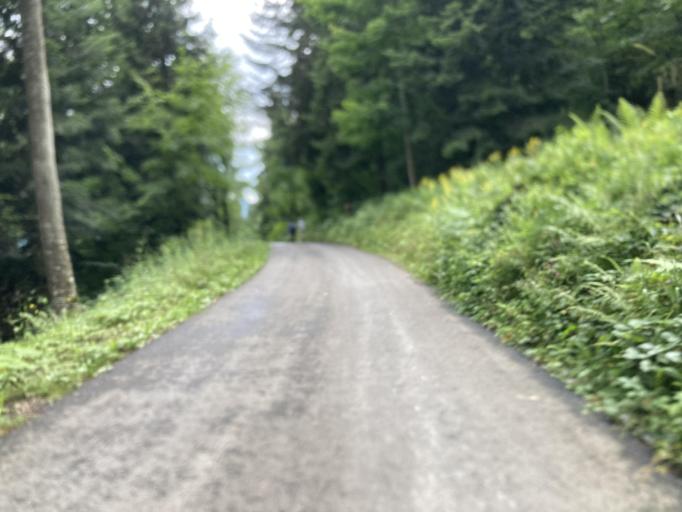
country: CH
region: Thurgau
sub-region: Muenchwilen District
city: Fischingen
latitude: 47.3690
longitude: 8.9435
